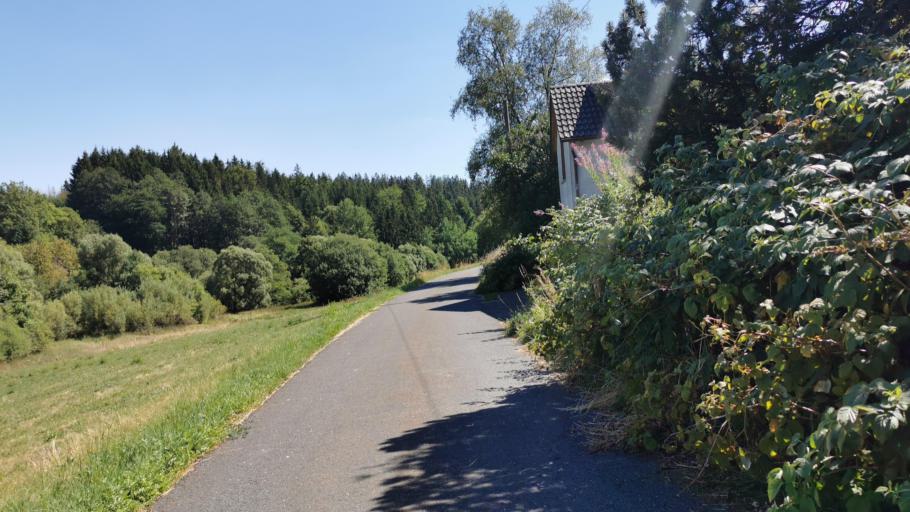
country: DE
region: Bavaria
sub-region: Upper Franconia
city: Tettau
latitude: 50.4192
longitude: 11.2909
